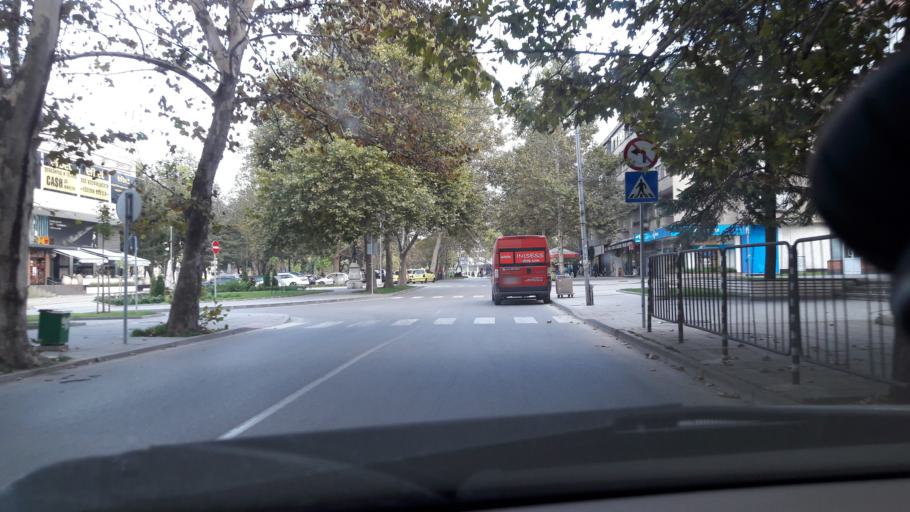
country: BG
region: Razgrad
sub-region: Obshtina Razgrad
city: Razgrad
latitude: 43.5254
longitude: 26.5214
